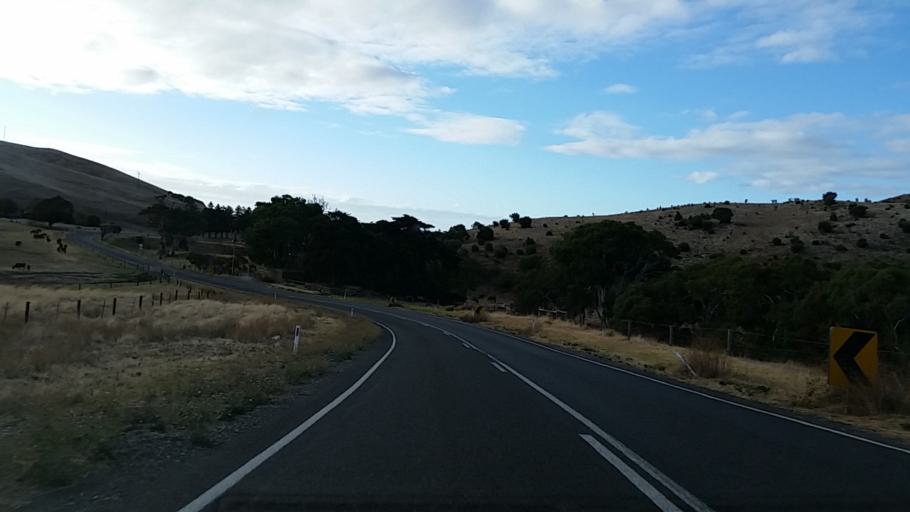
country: AU
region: South Australia
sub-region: Yankalilla
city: Normanville
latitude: -35.5341
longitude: 138.1943
